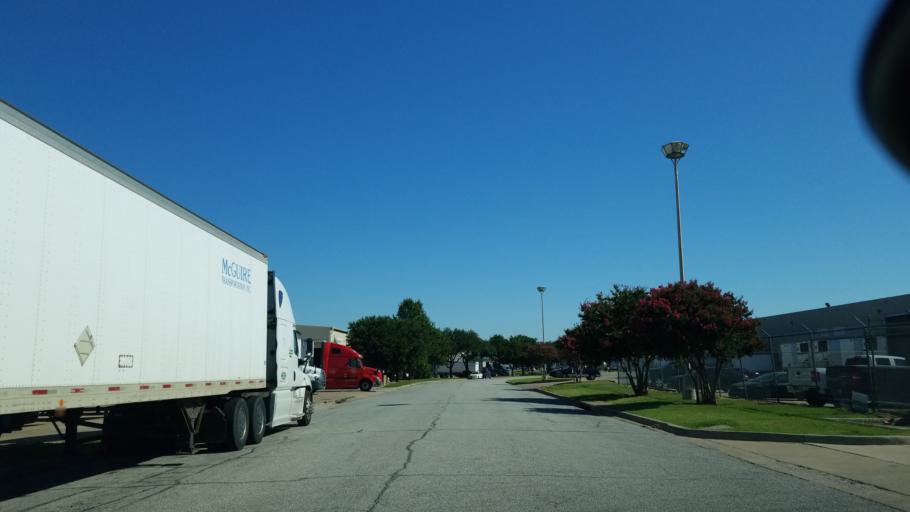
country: US
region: Texas
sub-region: Dallas County
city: Carrollton
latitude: 32.9555
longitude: -96.8839
